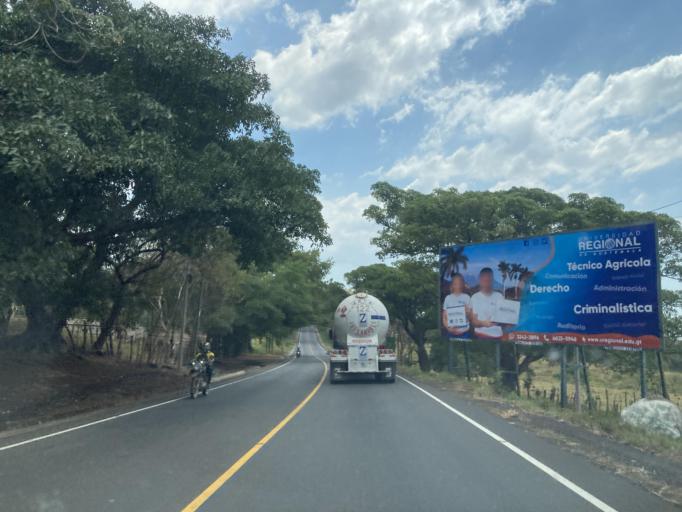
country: GT
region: Santa Rosa
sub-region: Municipio de Taxisco
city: Taxisco
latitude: 14.0813
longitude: -90.4888
